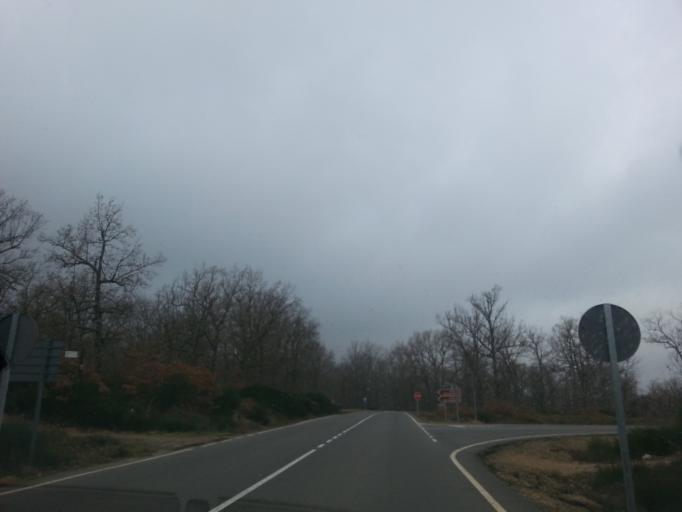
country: ES
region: Castille and Leon
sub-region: Provincia de Salamanca
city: La Alberca
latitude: 40.4892
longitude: -6.0920
